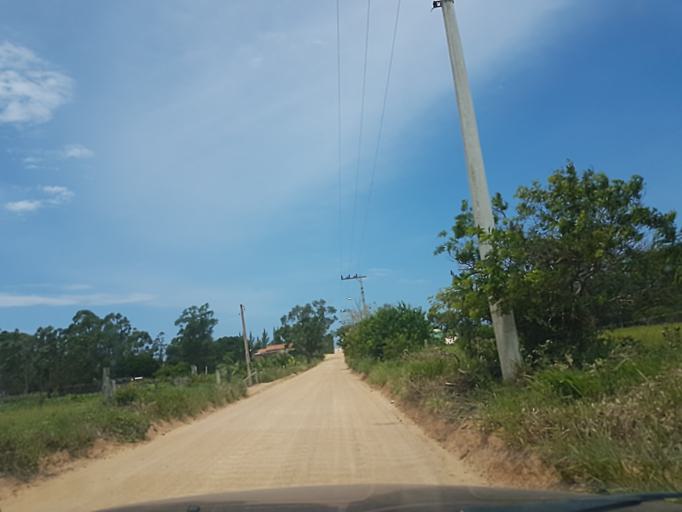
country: BR
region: Santa Catarina
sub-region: Jaguaruna
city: Jaguaruna
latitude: -28.6463
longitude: -48.9646
